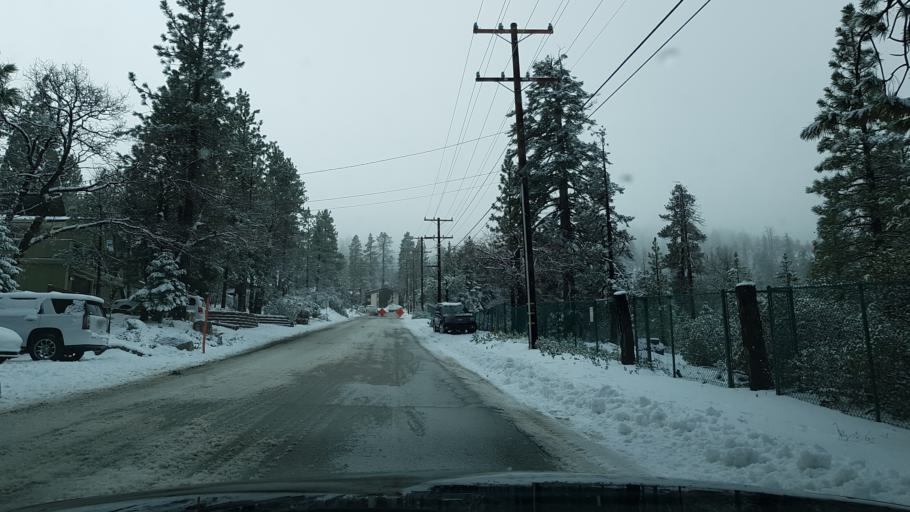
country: US
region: California
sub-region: San Bernardino County
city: Big Bear Lake
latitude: 34.2389
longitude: -116.8924
